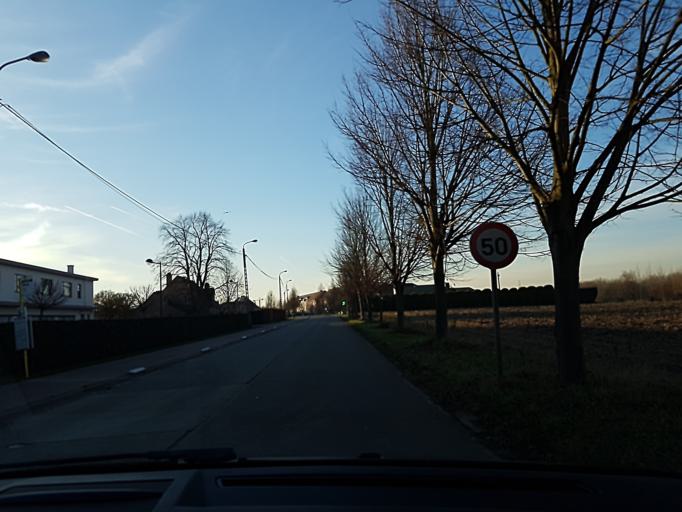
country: BE
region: Flanders
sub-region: Provincie Antwerpen
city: Bornem
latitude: 51.1011
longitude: 4.2539
